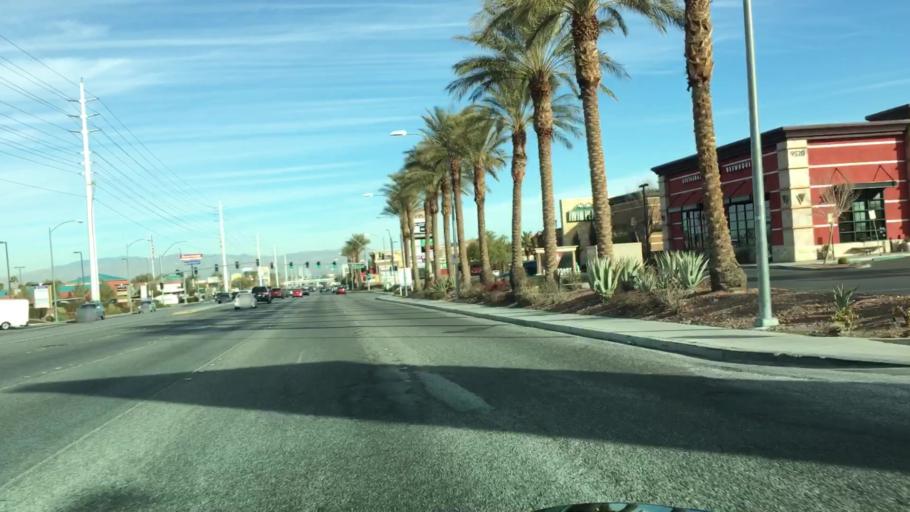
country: US
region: Nevada
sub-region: Clark County
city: Whitney
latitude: 36.0153
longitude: -115.1186
